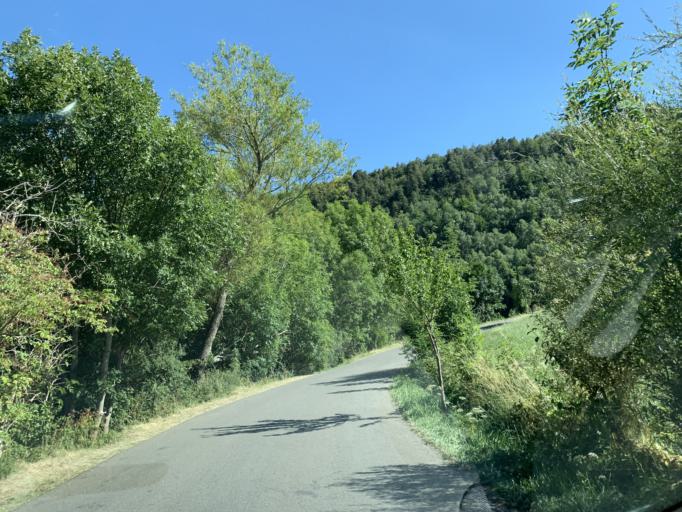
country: ES
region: Aragon
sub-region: Provincia de Huesca
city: Hoz de Jaca
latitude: 42.6948
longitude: -0.3254
